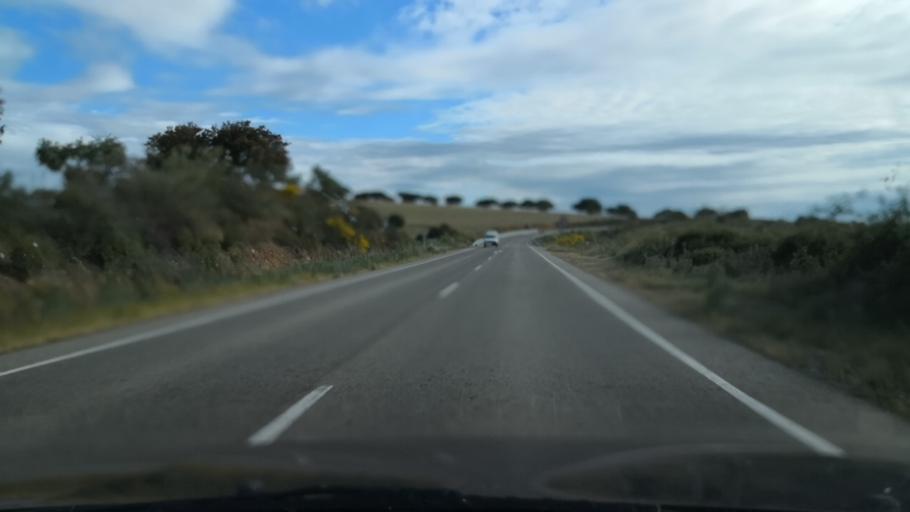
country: ES
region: Extremadura
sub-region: Provincia de Caceres
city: Perales del Puerto
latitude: 40.1130
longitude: -6.6706
